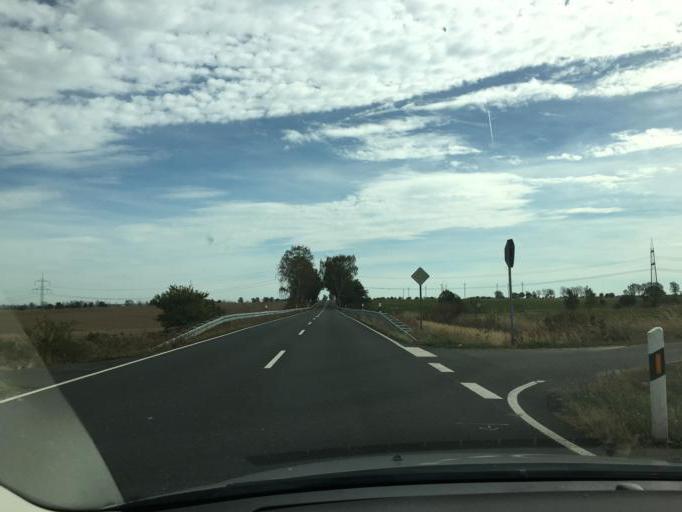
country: DE
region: Saxony
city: Lommatzsch
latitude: 51.2433
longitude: 13.3076
